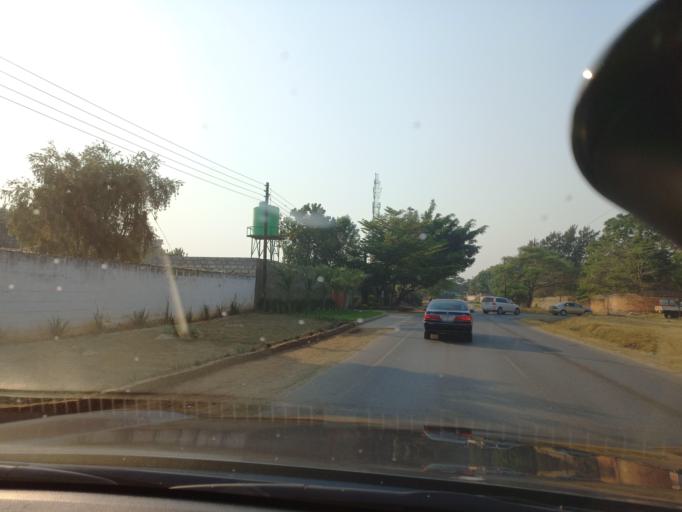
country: ZM
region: Lusaka
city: Lusaka
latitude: -15.4148
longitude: 28.3546
